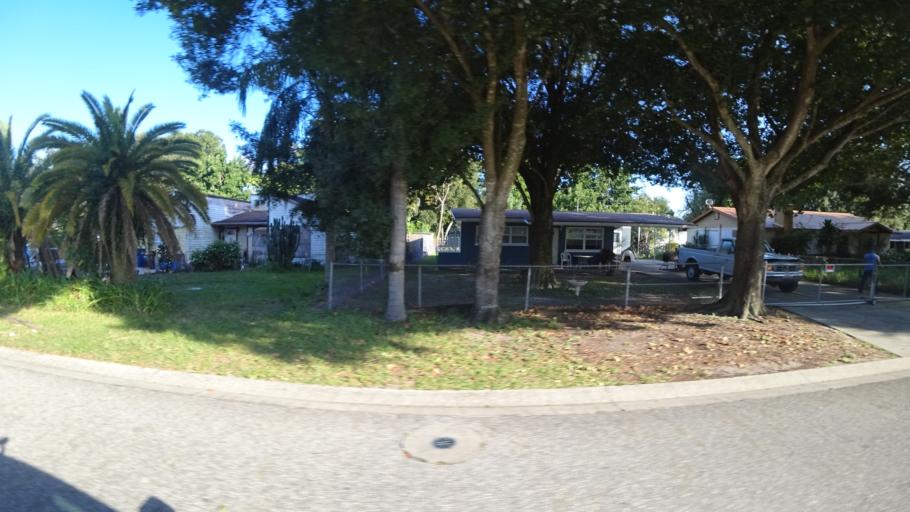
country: US
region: Florida
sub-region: Manatee County
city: West Samoset
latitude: 27.4716
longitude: -82.5602
